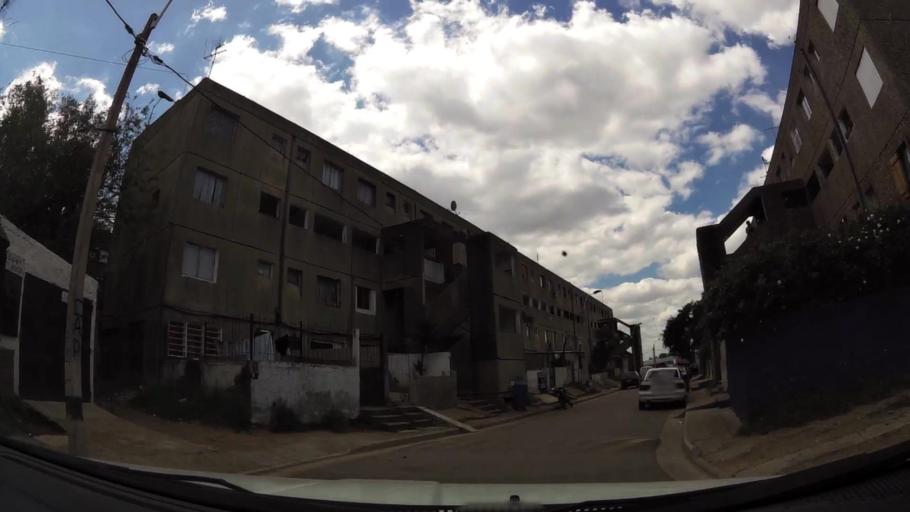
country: UY
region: Canelones
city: La Paz
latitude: -34.8202
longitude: -56.2482
